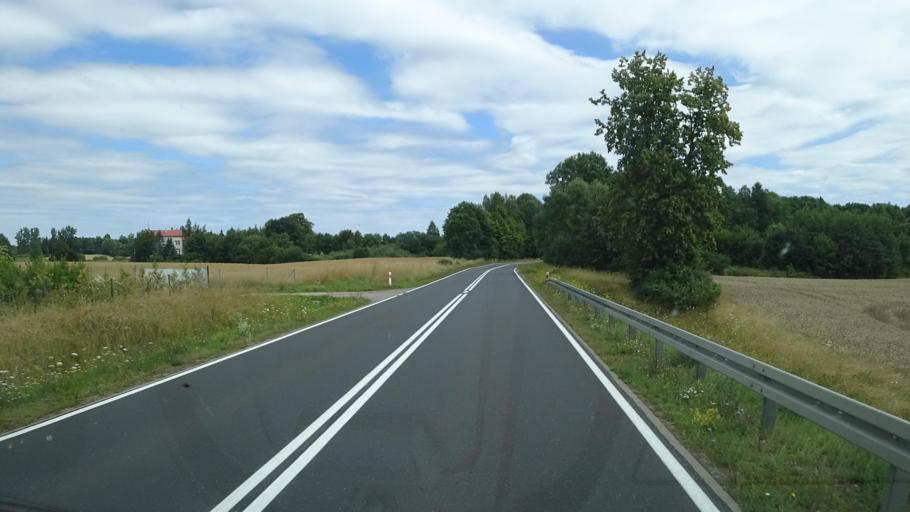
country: PL
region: Warmian-Masurian Voivodeship
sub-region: Powiat elcki
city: Elk
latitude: 53.7995
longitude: 22.2419
